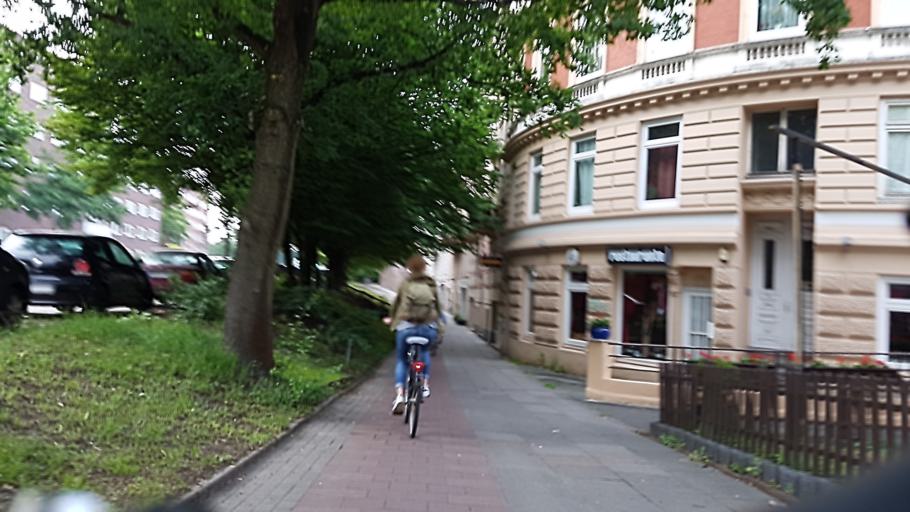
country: DE
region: Hamburg
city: Hamburg
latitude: 53.5890
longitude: 10.0157
